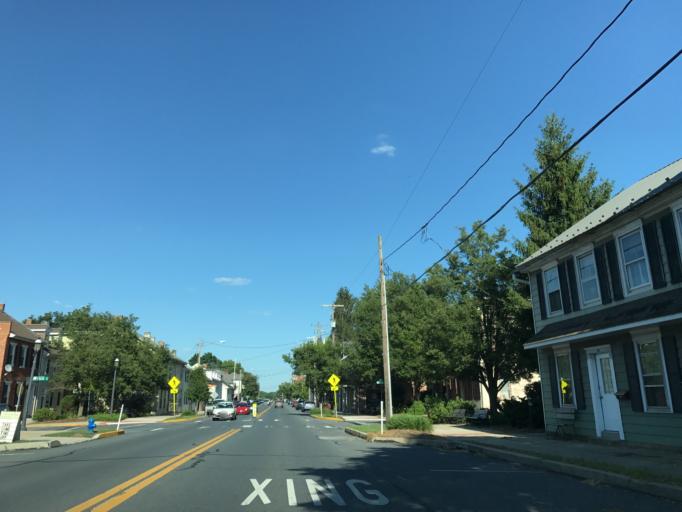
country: US
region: Pennsylvania
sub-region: Lancaster County
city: Mount Joy
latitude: 40.1092
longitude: -76.4978
